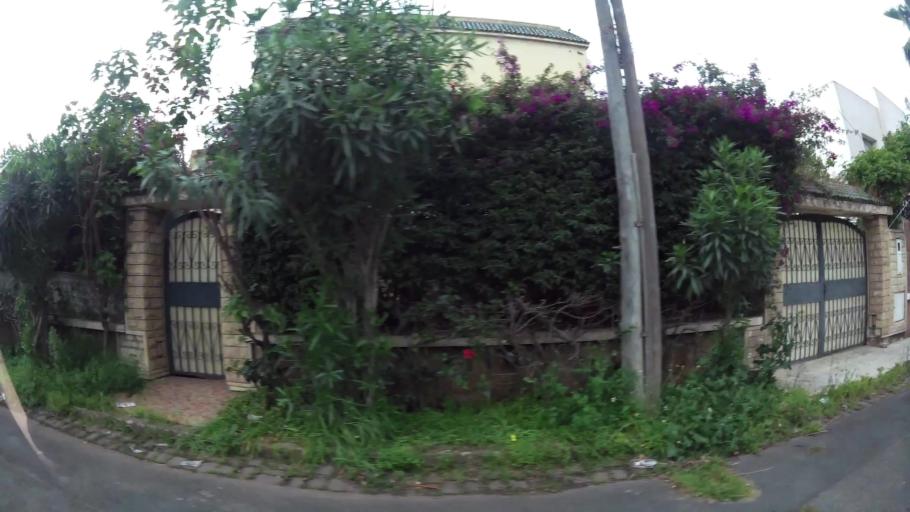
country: MA
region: Grand Casablanca
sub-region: Casablanca
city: Casablanca
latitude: 33.5670
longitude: -7.6425
